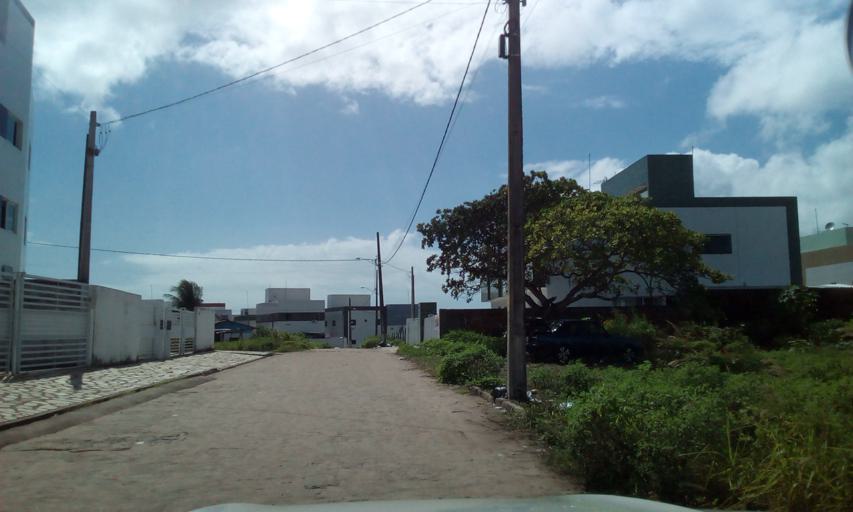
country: BR
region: Paraiba
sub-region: Conde
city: Conde
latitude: -7.2194
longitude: -34.8310
